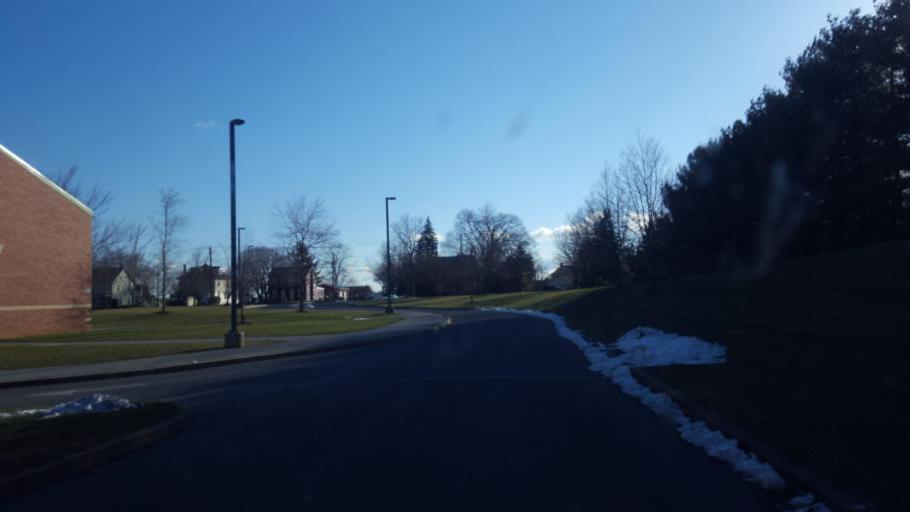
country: US
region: Pennsylvania
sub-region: Lancaster County
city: Lampeter
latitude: 40.0520
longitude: -76.2148
